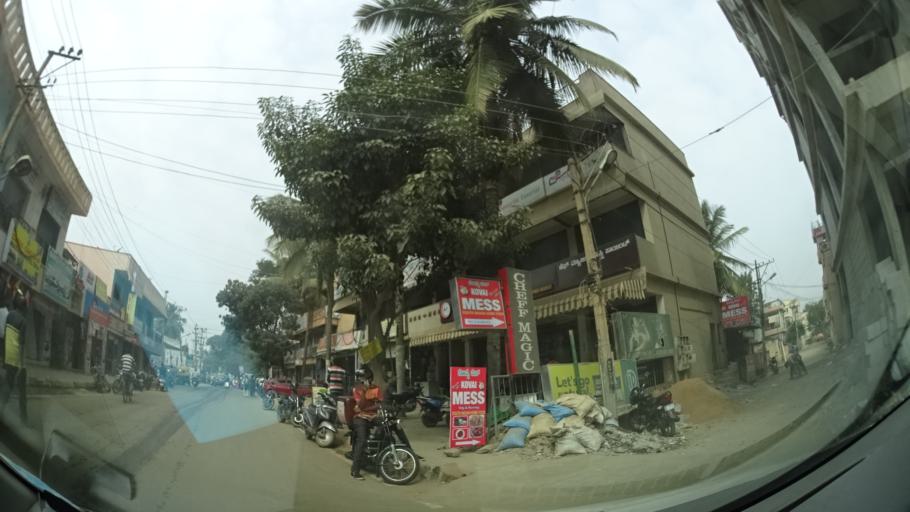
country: IN
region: Karnataka
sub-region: Bangalore Rural
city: Hoskote
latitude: 12.9692
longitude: 77.7545
